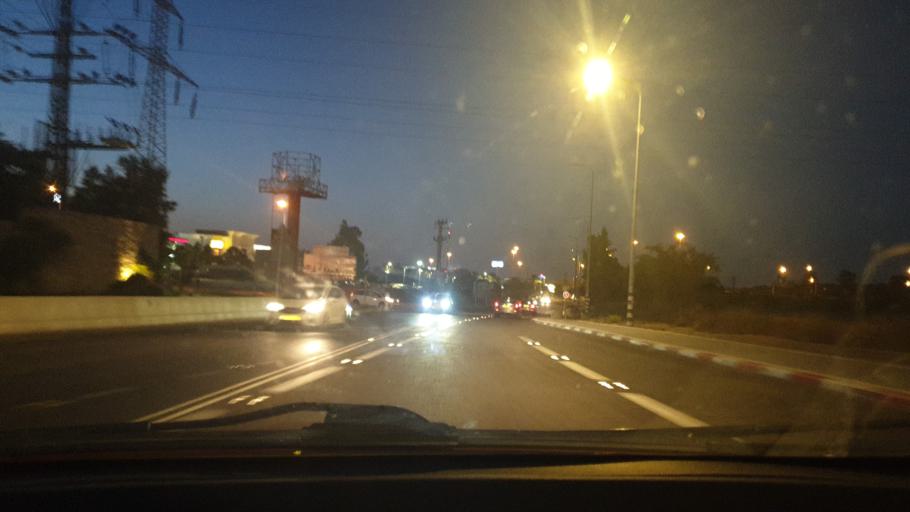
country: IL
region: Central District
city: Bene 'Ayish
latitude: 31.7967
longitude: 34.7607
